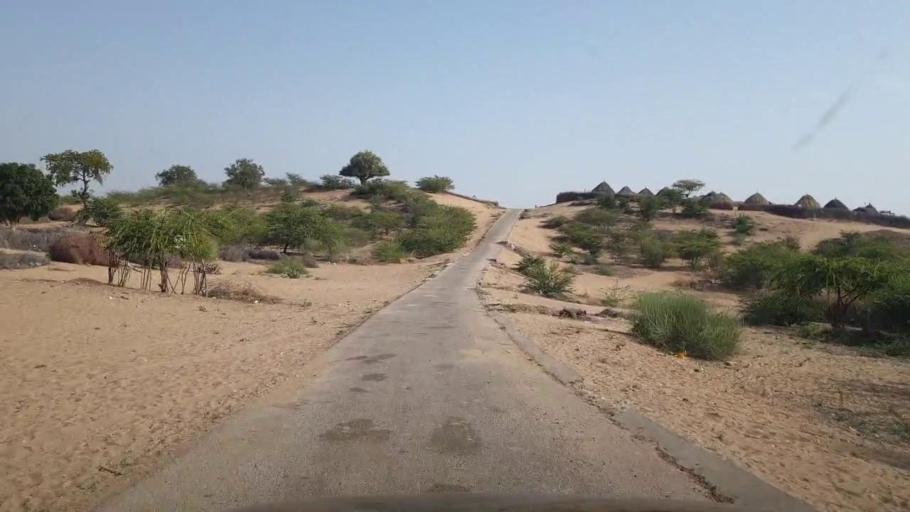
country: PK
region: Sindh
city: Islamkot
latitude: 25.1219
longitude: 70.5111
